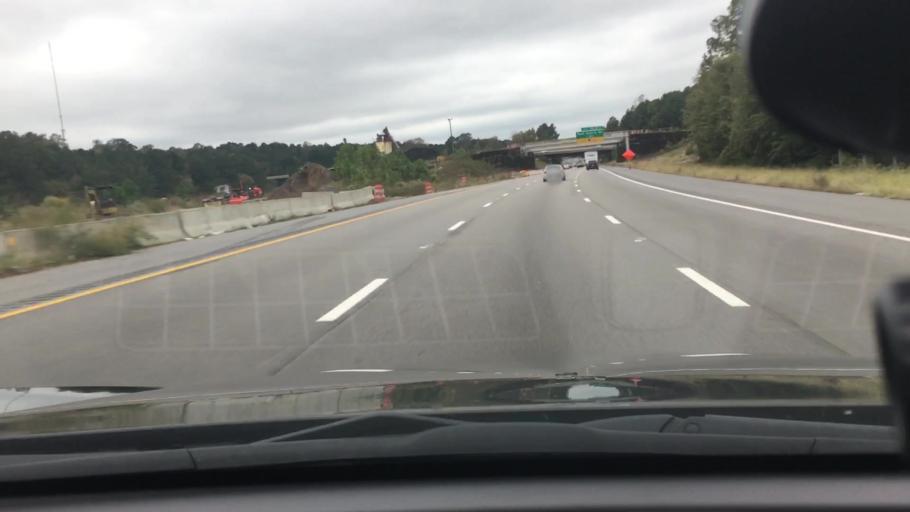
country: US
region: North Carolina
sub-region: Wake County
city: Garner
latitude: 35.7536
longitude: -78.5898
